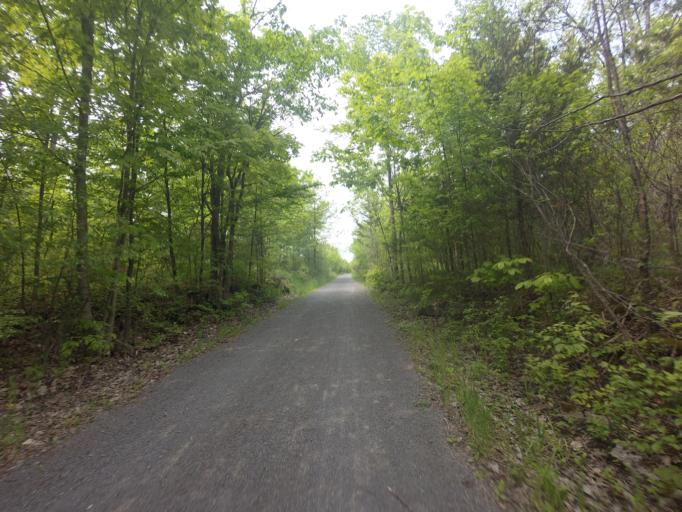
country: CA
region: Ontario
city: Kingston
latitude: 44.3267
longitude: -76.5887
